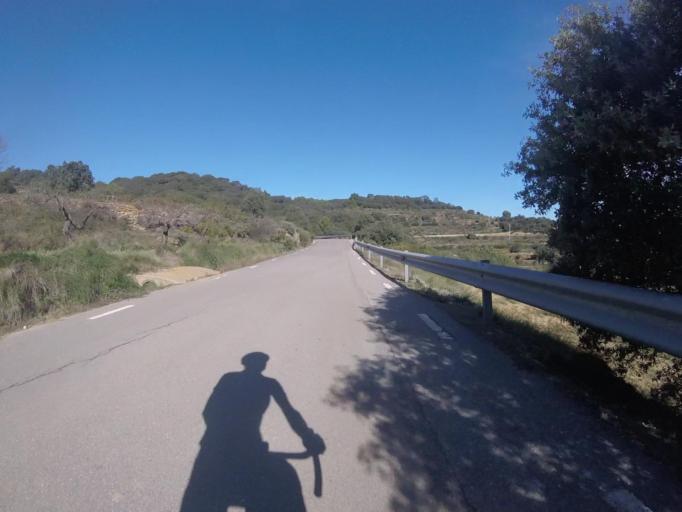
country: ES
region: Valencia
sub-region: Provincia de Castello
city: Sarratella
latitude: 40.3042
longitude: 0.0312
